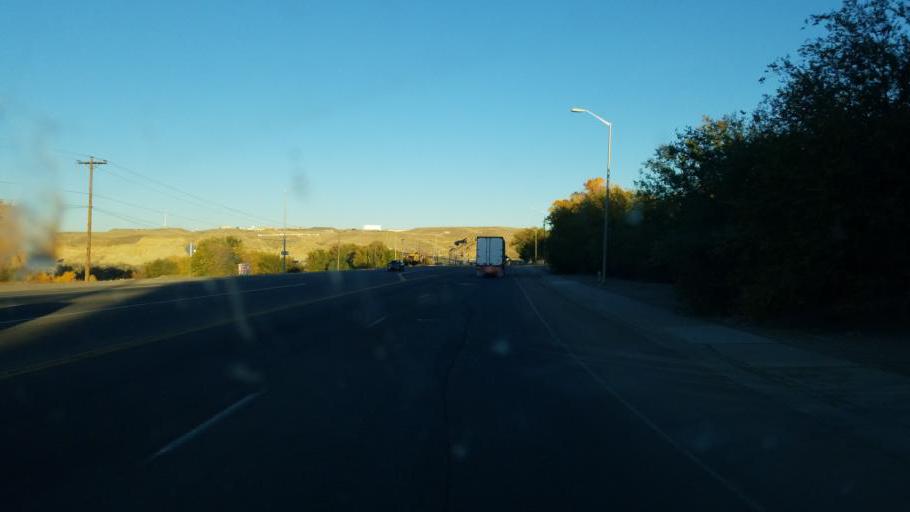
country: US
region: New Mexico
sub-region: San Juan County
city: Farmington
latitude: 36.7339
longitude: -108.2454
